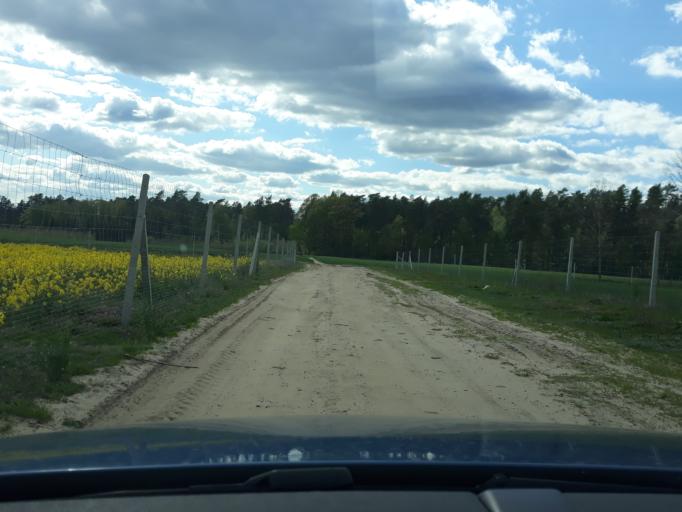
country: PL
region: Pomeranian Voivodeship
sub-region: Powiat czluchowski
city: Czluchow
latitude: 53.7194
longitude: 17.3482
